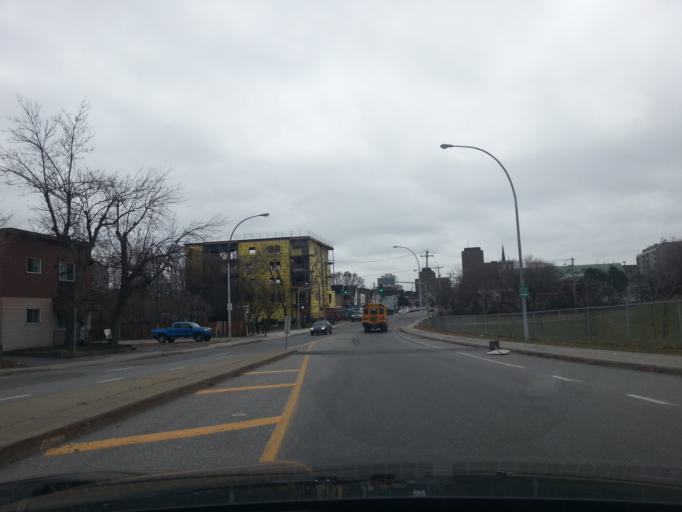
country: CA
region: Ontario
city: Ottawa
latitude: 45.4363
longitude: -75.7224
